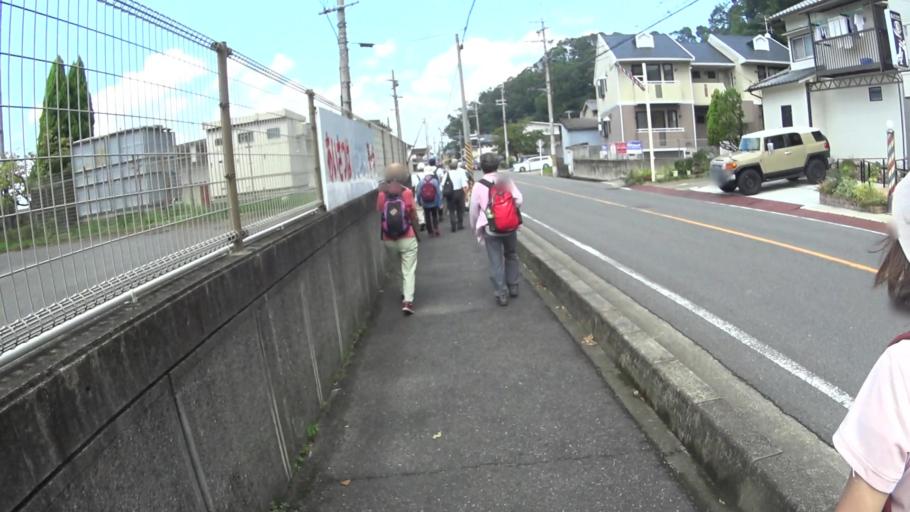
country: JP
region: Nara
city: Sakurai
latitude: 34.5032
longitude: 135.8529
